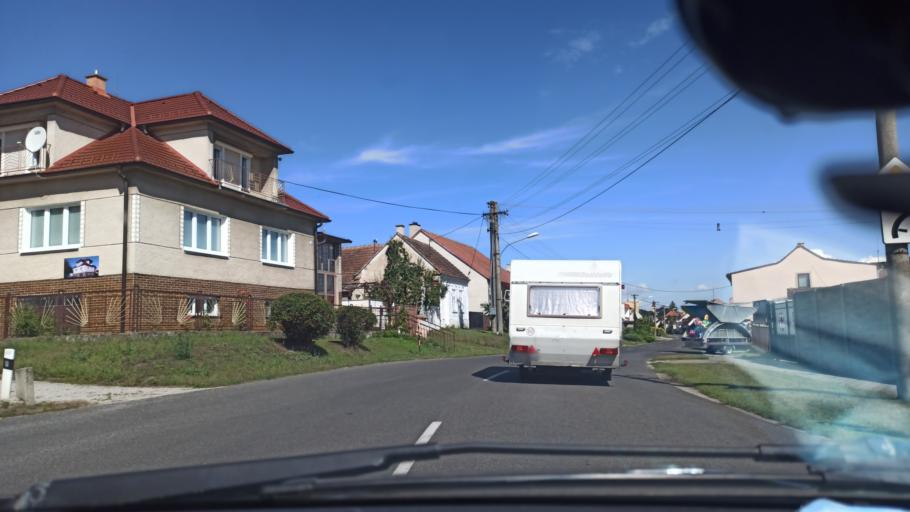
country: SK
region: Trnavsky
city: Gbely
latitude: 48.6712
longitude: 17.2019
